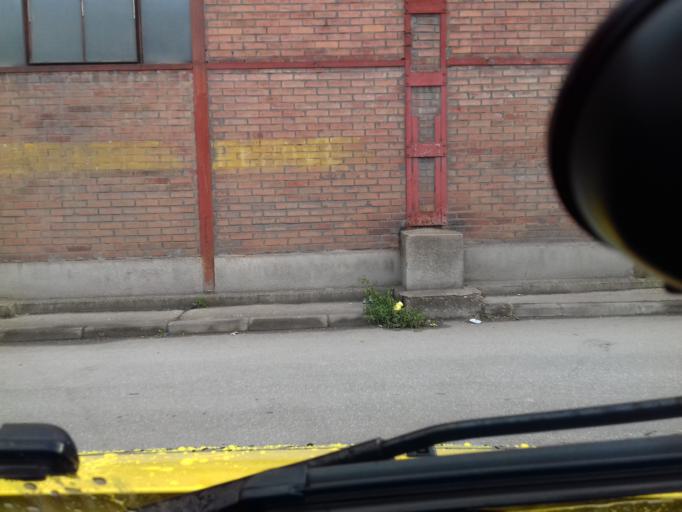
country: BA
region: Federation of Bosnia and Herzegovina
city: Zenica
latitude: 44.2087
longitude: 17.9003
